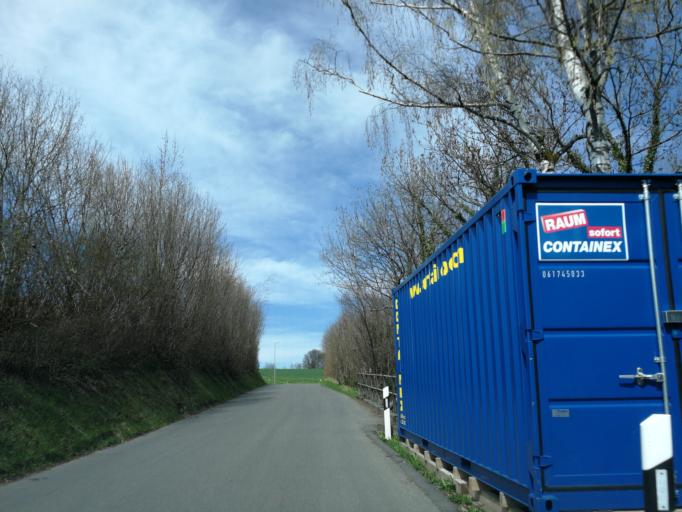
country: CH
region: Zurich
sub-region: Bezirk Meilen
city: Meilen
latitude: 47.2769
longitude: 8.6379
